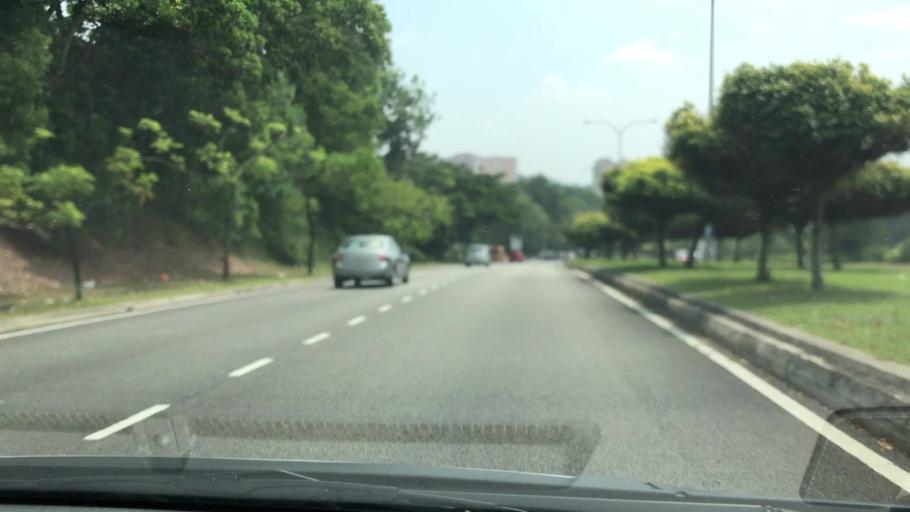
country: MY
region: Putrajaya
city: Putrajaya
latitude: 3.0002
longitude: 101.6649
